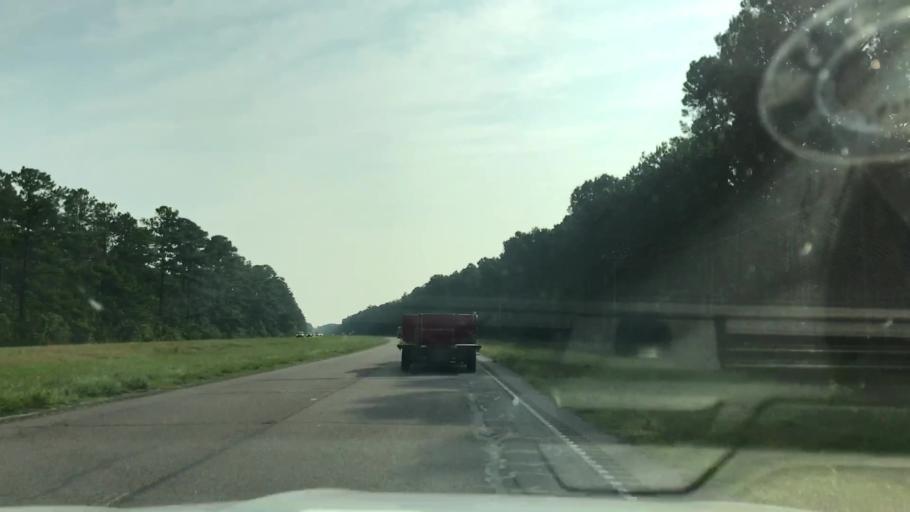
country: US
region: South Carolina
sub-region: Charleston County
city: Awendaw
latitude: 33.0790
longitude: -79.5049
